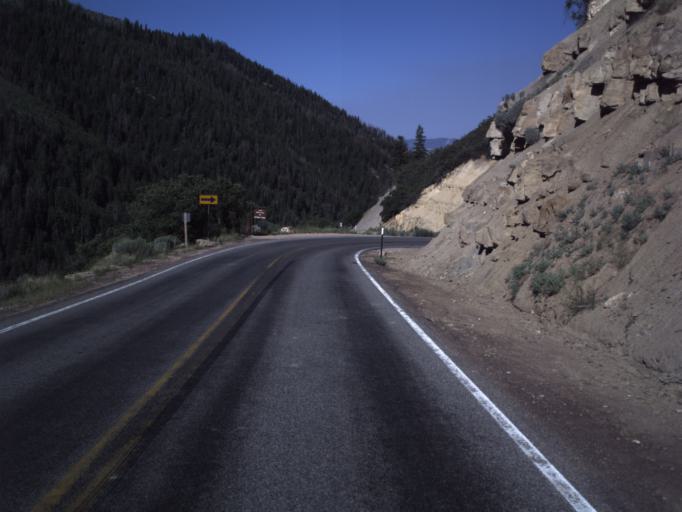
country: US
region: Utah
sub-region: Sanpete County
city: Fairview
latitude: 39.6483
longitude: -111.3680
